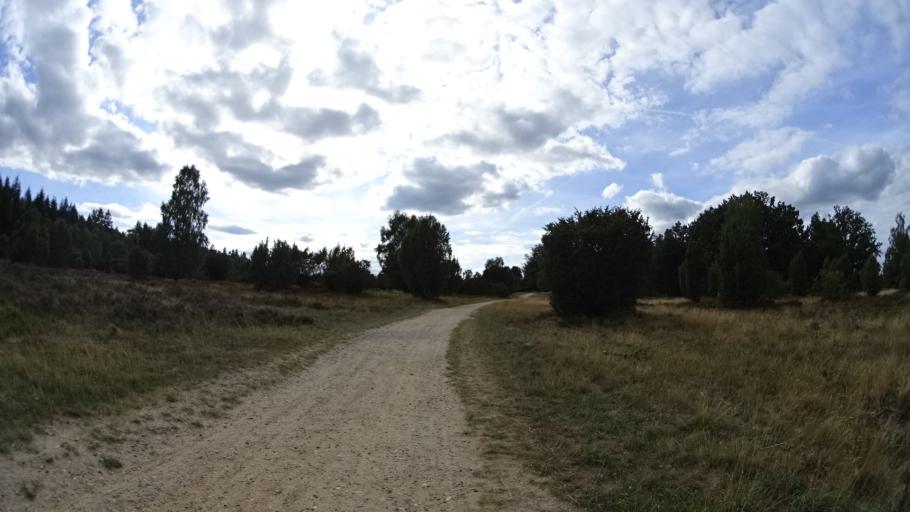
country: DE
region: Lower Saxony
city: Undeloh
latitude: 53.1655
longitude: 9.9503
